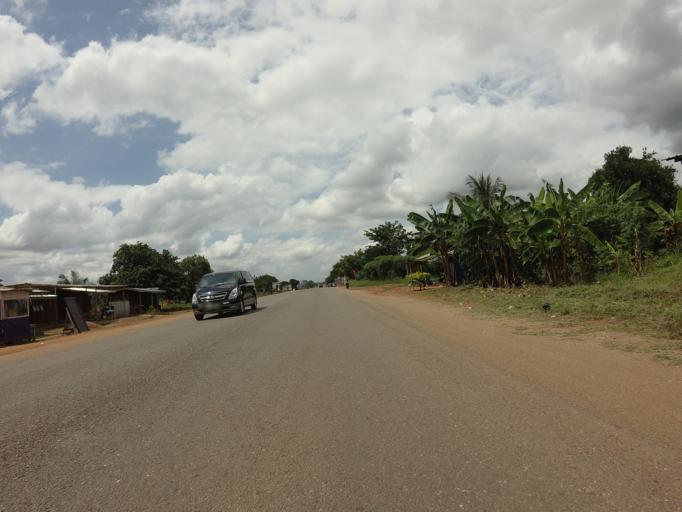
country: GH
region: Eastern
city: Aburi
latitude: 5.8441
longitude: -0.1150
